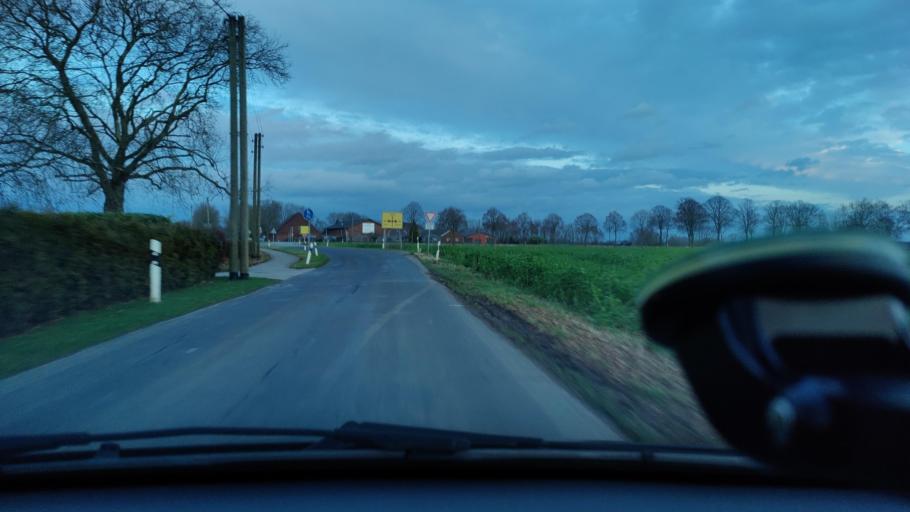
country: DE
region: North Rhine-Westphalia
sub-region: Regierungsbezirk Dusseldorf
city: Xanten
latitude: 51.6787
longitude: 6.4147
